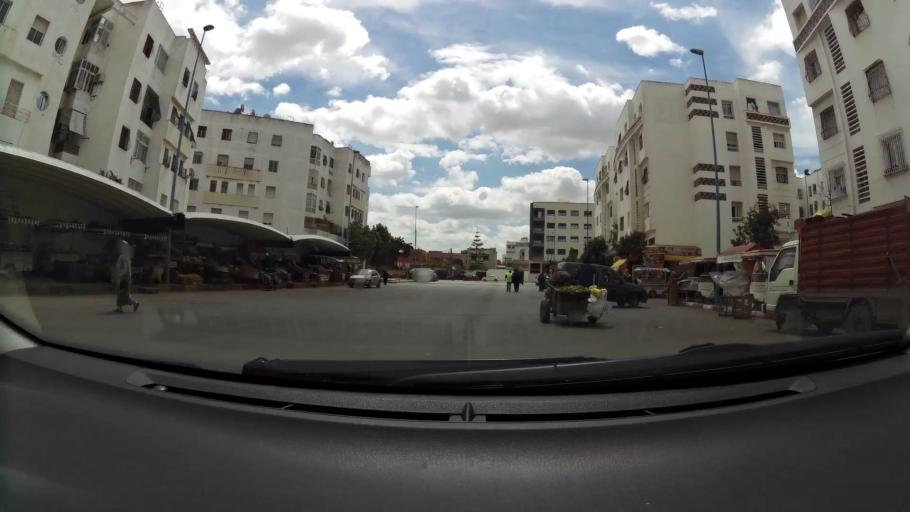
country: MA
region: Grand Casablanca
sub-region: Casablanca
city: Casablanca
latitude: 33.6104
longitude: -7.5433
